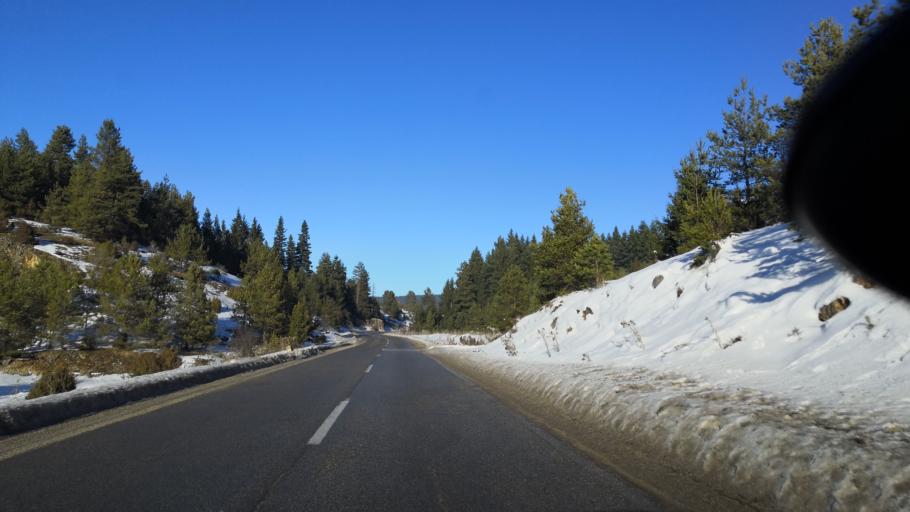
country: BA
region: Republika Srpska
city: Sokolac
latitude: 43.9893
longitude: 18.8719
